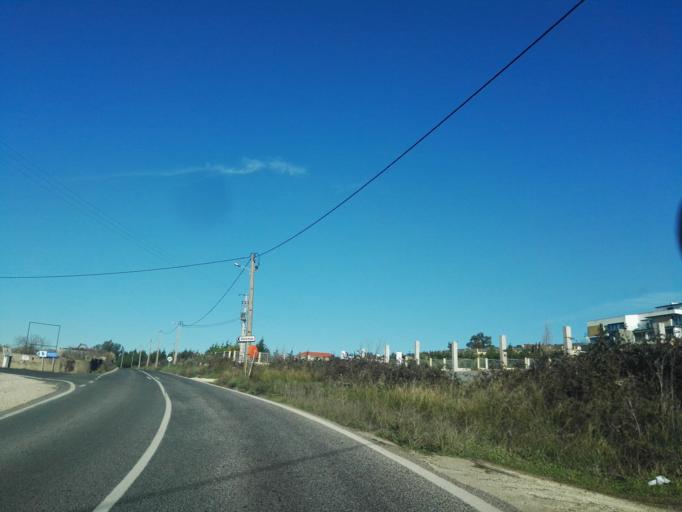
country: PT
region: Lisbon
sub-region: Loures
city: Loures
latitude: 38.8775
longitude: -9.1848
